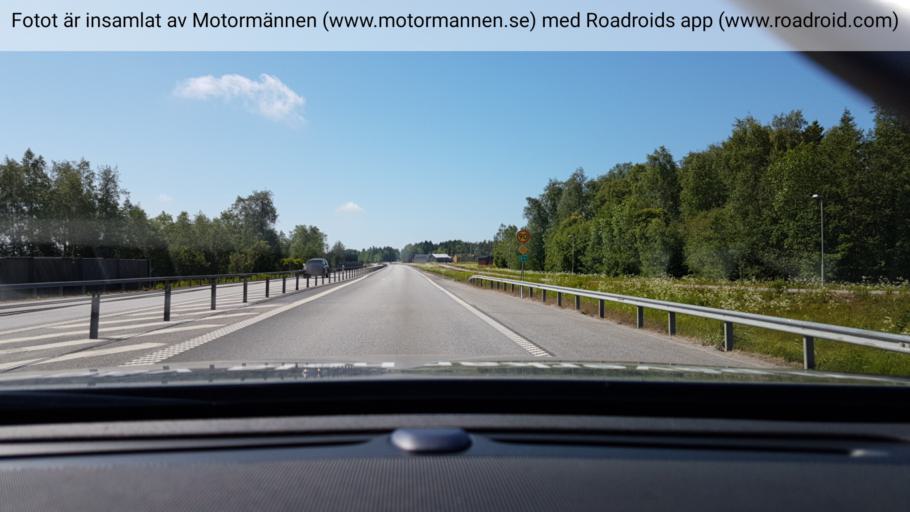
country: SE
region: Vaesterbotten
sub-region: Umea Kommun
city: Roback
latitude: 63.7767
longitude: 20.1885
